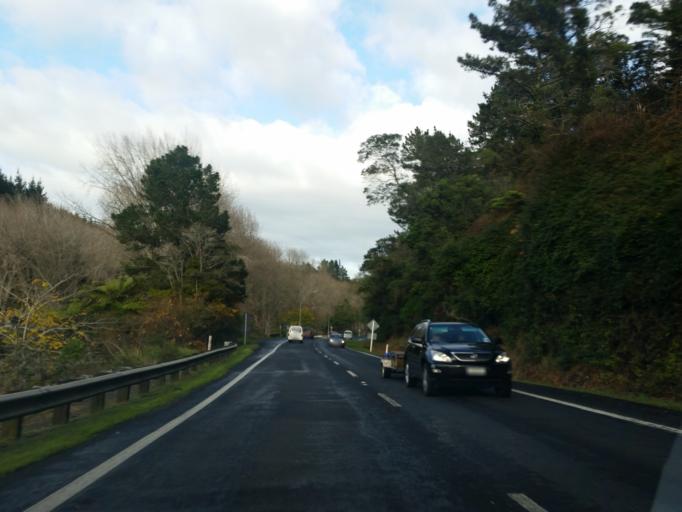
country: NZ
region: Waikato
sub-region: Hauraki District
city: Waihi
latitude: -37.4114
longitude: 175.7726
